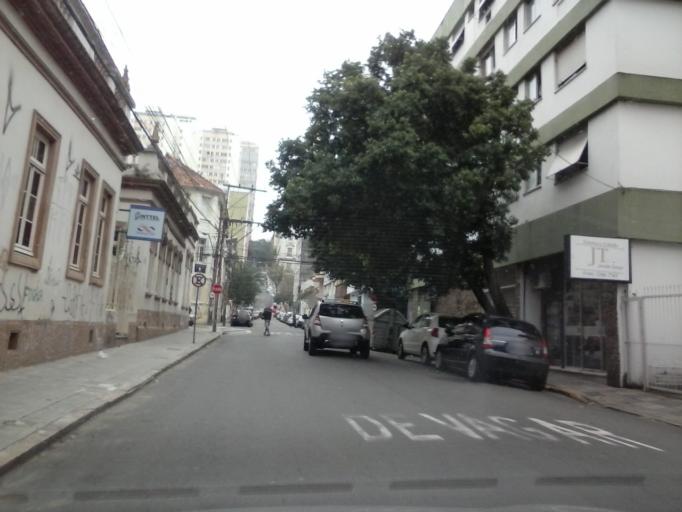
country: BR
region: Rio Grande do Sul
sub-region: Porto Alegre
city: Porto Alegre
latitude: -30.0363
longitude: -51.2319
